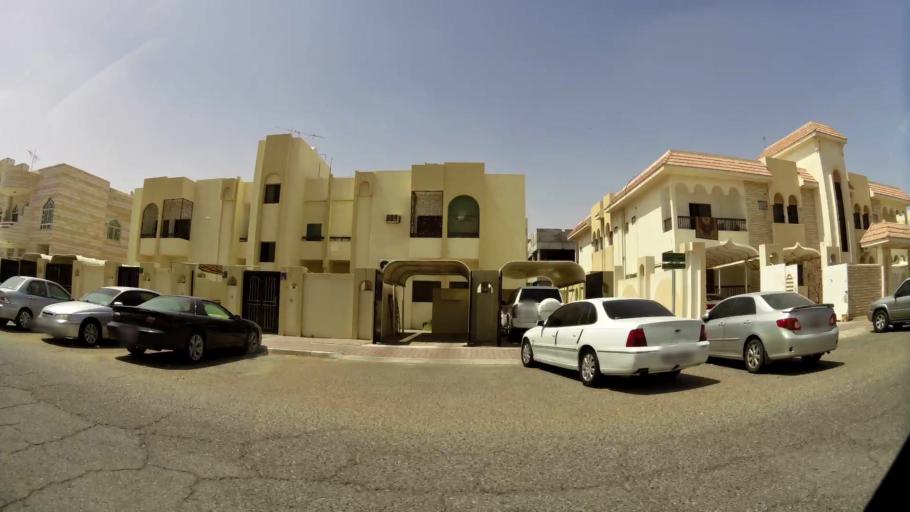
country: AE
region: Abu Dhabi
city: Al Ain
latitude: 24.2381
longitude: 55.7178
